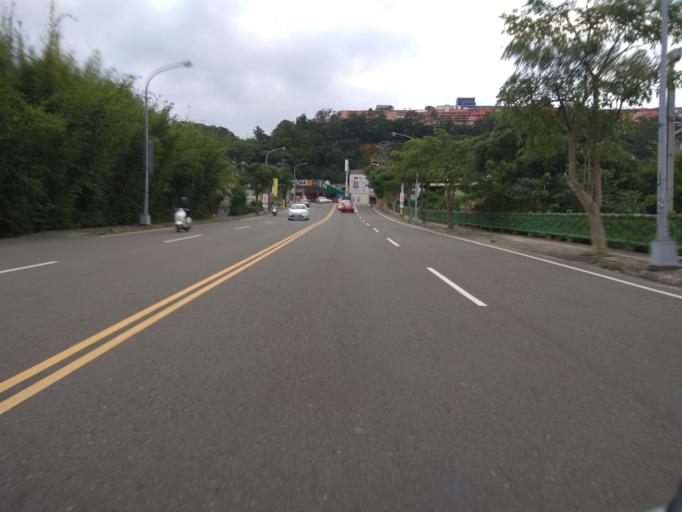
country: TW
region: Taiwan
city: Daxi
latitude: 24.8553
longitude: 121.2045
